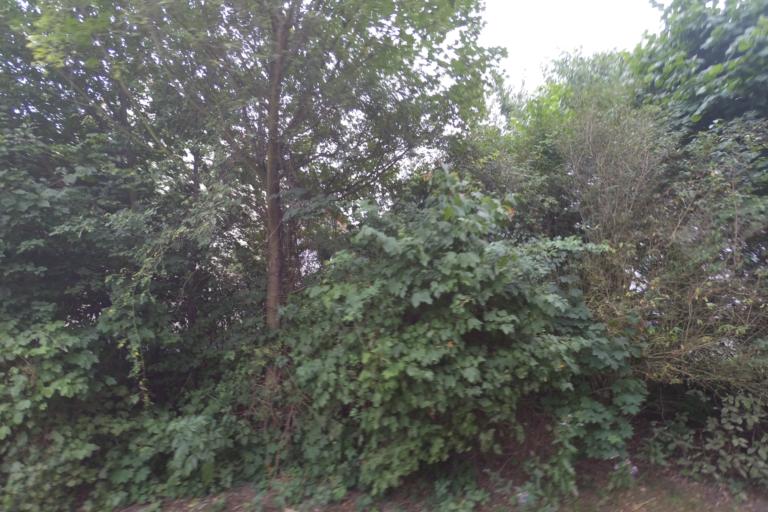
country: DE
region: Rheinland-Pfalz
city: Neuhofen
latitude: 49.4451
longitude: 8.4243
